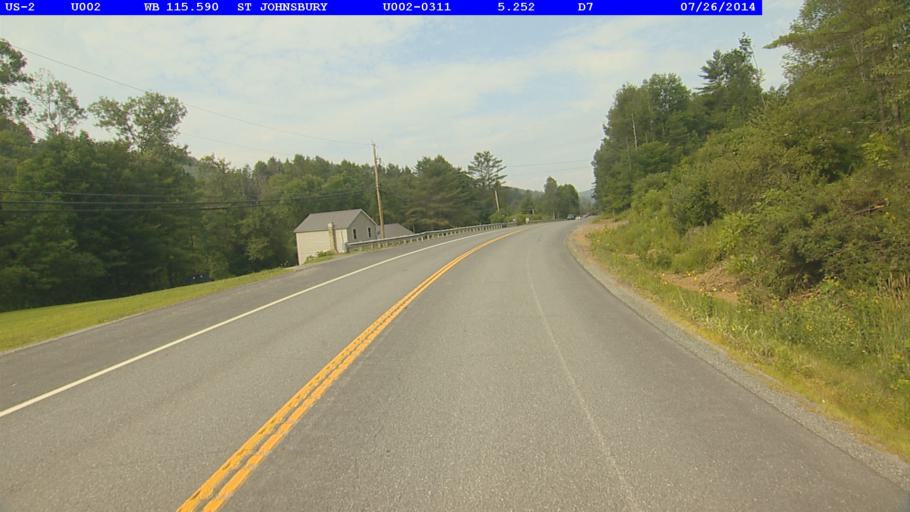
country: US
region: Vermont
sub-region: Caledonia County
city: Saint Johnsbury
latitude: 44.4218
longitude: -71.9830
